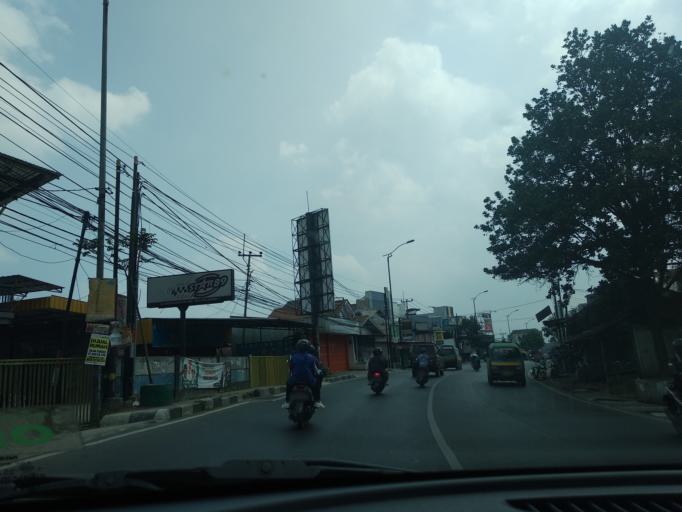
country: ID
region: West Java
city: Cimahi
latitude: -6.8691
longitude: 107.5280
